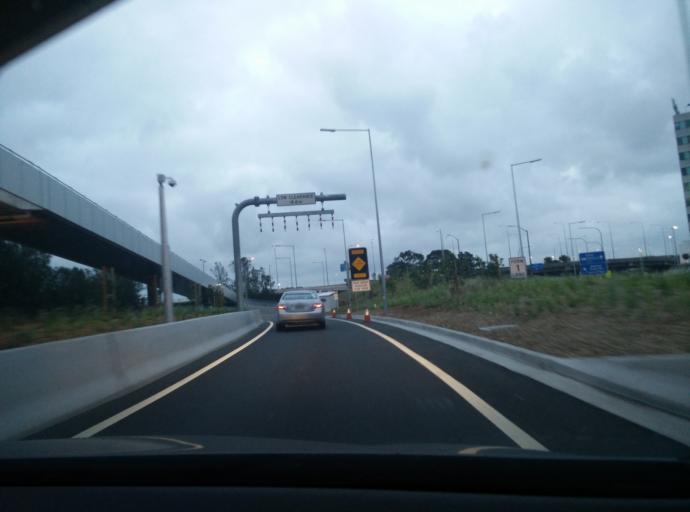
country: AU
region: New South Wales
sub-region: Rockdale
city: Arncliffe
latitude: -33.9351
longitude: 151.1627
